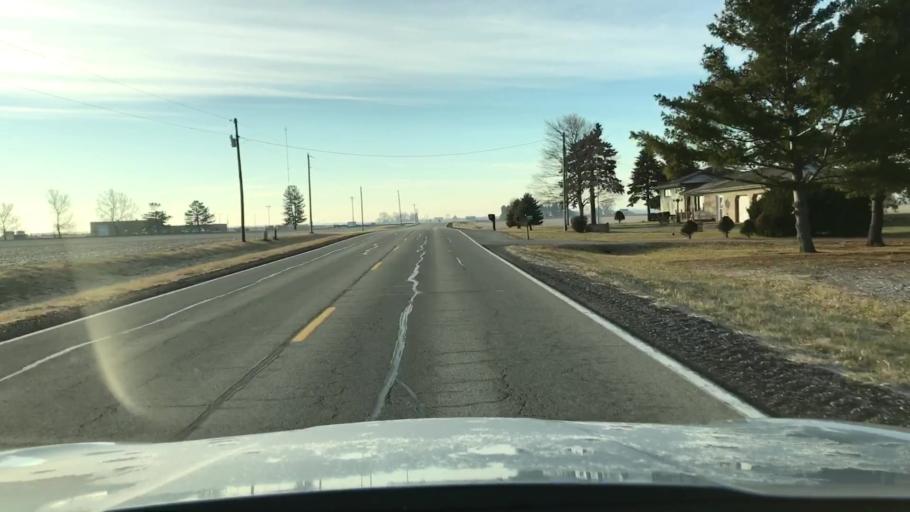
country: US
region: Illinois
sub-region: McLean County
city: Hudson
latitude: 40.5863
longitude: -88.9448
